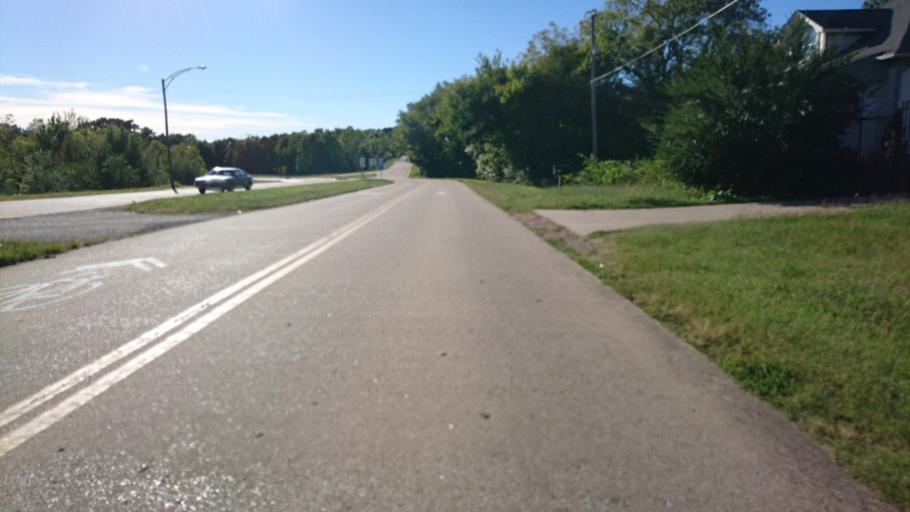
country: US
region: Missouri
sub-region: Jasper County
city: Carthage
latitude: 37.1766
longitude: -94.3421
